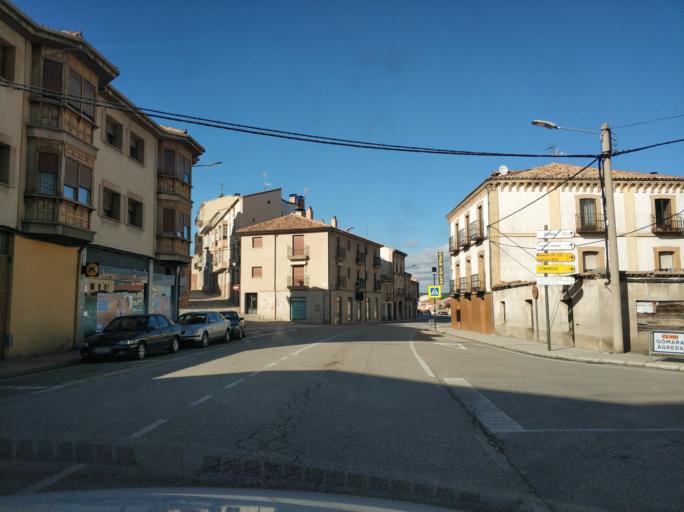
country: ES
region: Castille and Leon
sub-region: Provincia de Soria
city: Almazan
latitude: 41.4854
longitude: -2.5310
